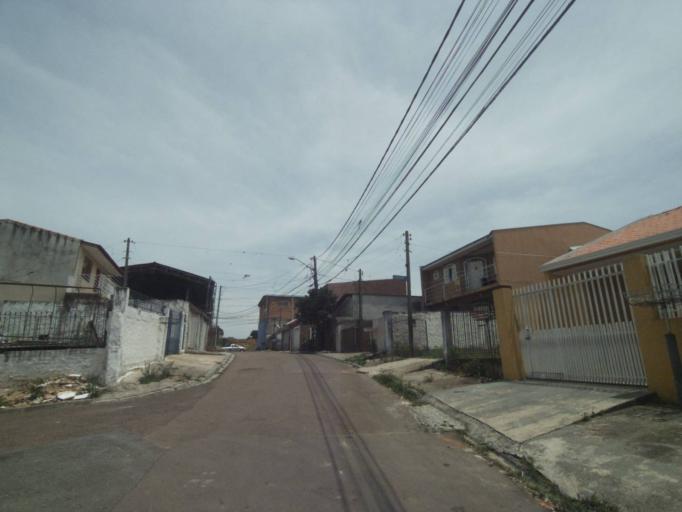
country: BR
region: Parana
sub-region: Curitiba
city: Curitiba
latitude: -25.5011
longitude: -49.3406
